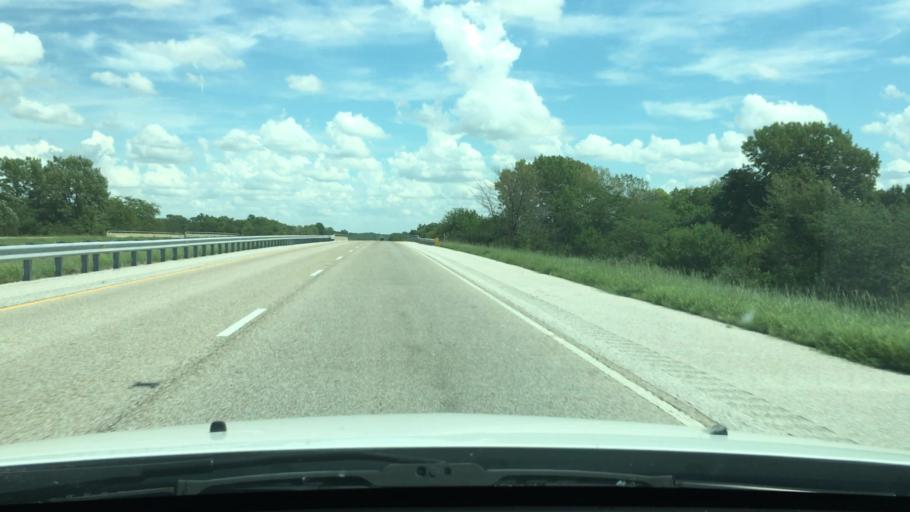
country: US
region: Illinois
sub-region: Scott County
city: Winchester
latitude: 39.6811
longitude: -90.4301
